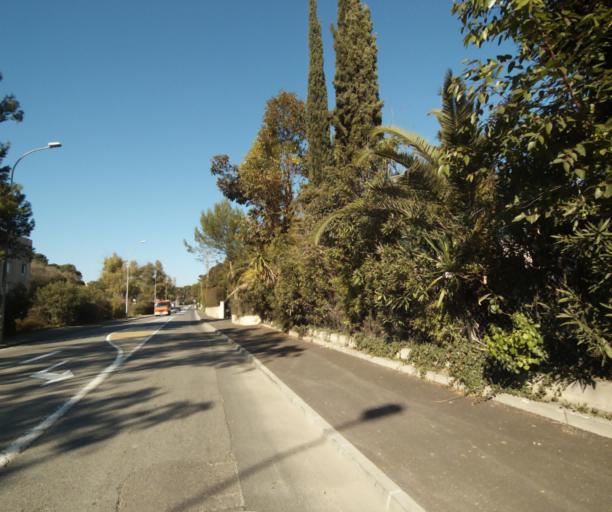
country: FR
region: Provence-Alpes-Cote d'Azur
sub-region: Departement des Alpes-Maritimes
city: Biot
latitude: 43.5983
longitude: 7.1029
